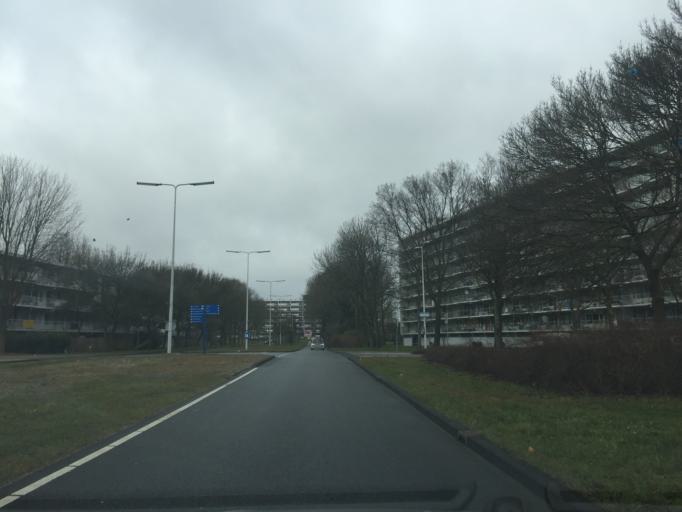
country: NL
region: South Holland
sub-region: Gemeente Leiden
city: Leiden
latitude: 52.1726
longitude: 4.5101
